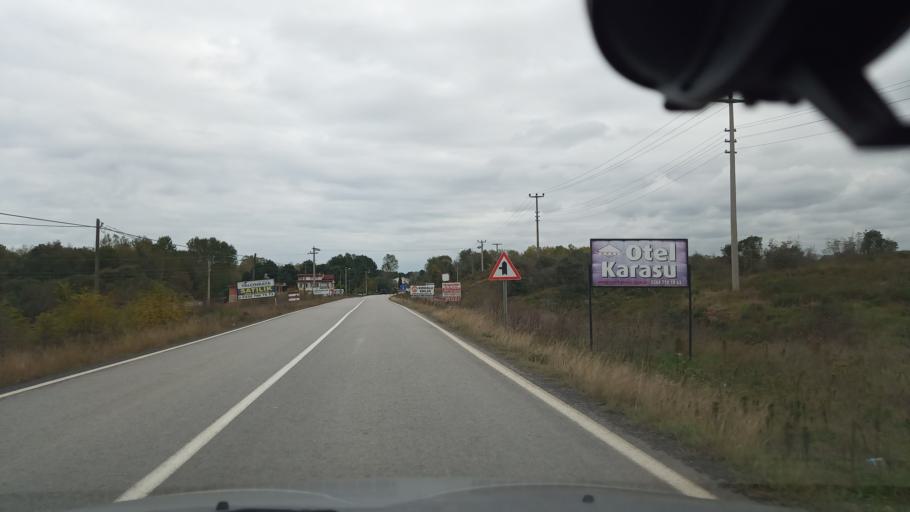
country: TR
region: Sakarya
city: Karasu
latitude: 41.1191
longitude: 30.6068
